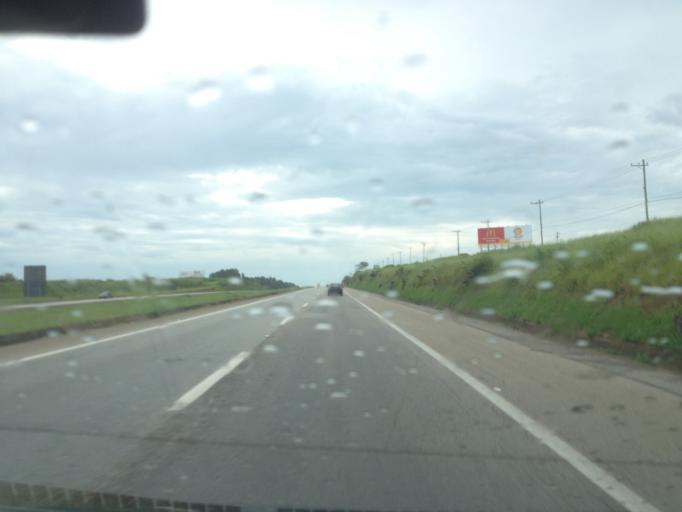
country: BR
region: Sao Paulo
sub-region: Porto Feliz
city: Porto Feliz
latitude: -23.3405
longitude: -47.5366
